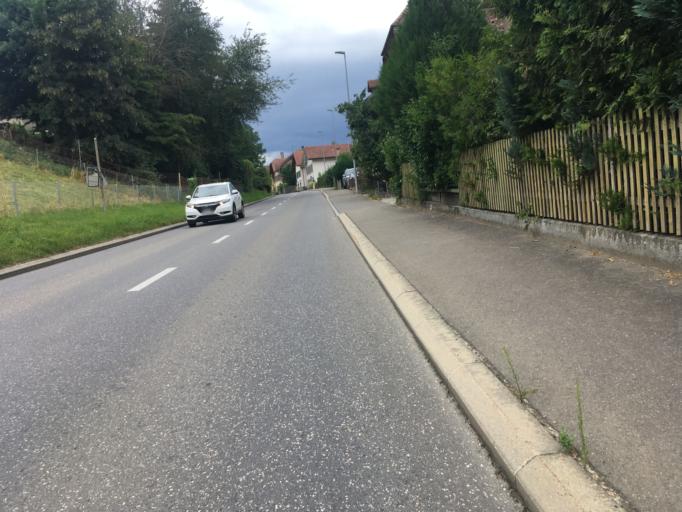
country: CH
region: Vaud
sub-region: Broye-Vully District
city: Payerne
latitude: 46.8722
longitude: 6.9328
